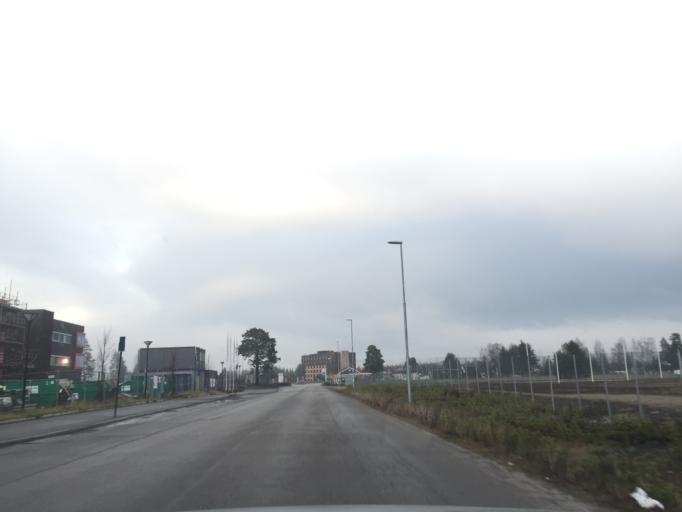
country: NO
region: Hedmark
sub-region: Elverum
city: Elverum
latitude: 60.8801
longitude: 11.5381
